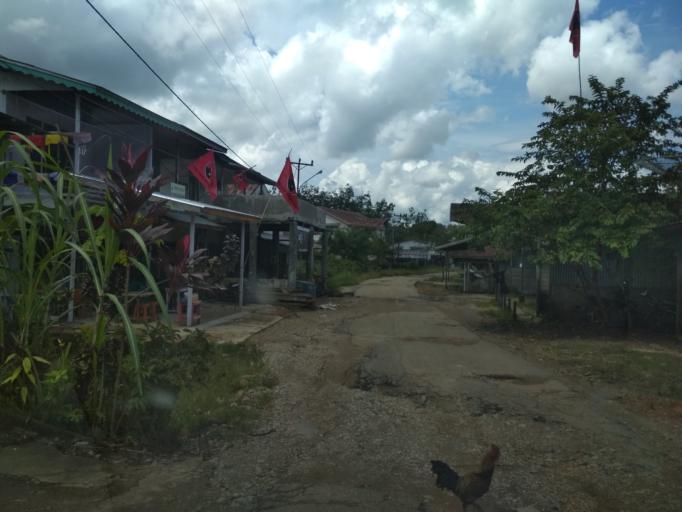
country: ID
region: West Kalimantan
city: Bengkayang
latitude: 0.7473
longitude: 110.1076
